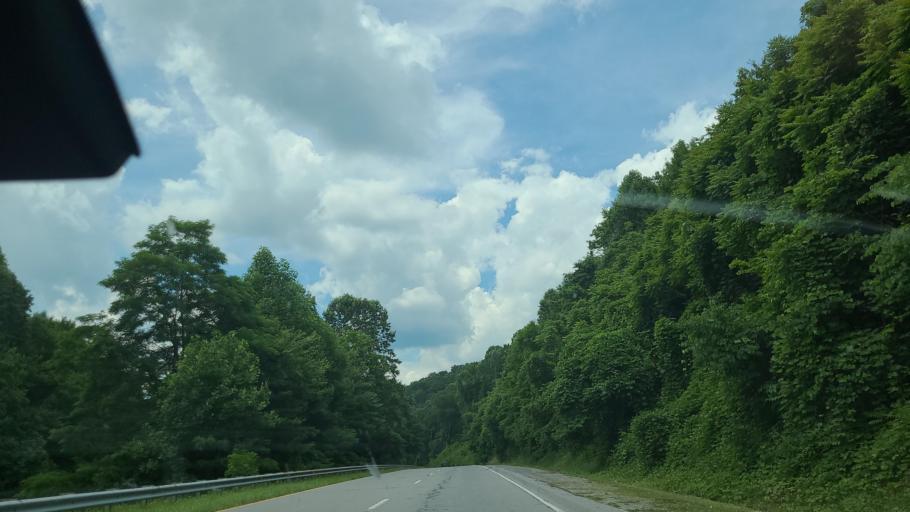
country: US
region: Georgia
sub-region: Fannin County
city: McCaysville
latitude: 35.0151
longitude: -84.2842
